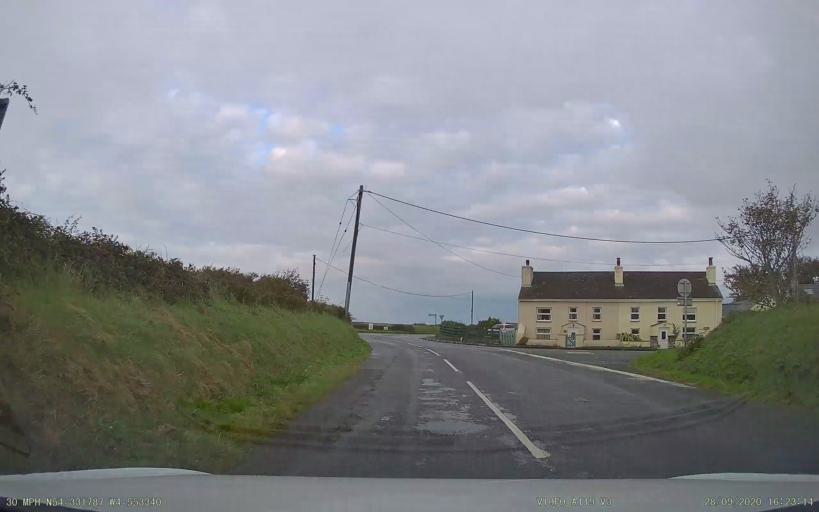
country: IM
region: Ramsey
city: Ramsey
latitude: 54.3318
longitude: -4.5533
